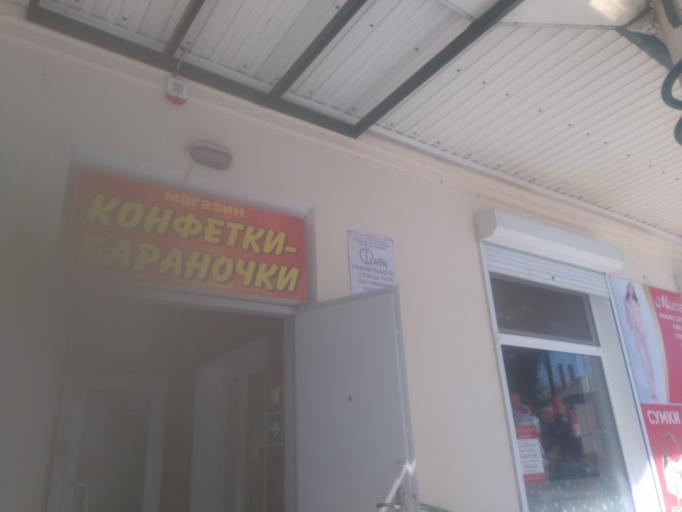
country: RU
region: Krasnodarskiy
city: Fastovetskaya
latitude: 45.9190
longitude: 40.1555
